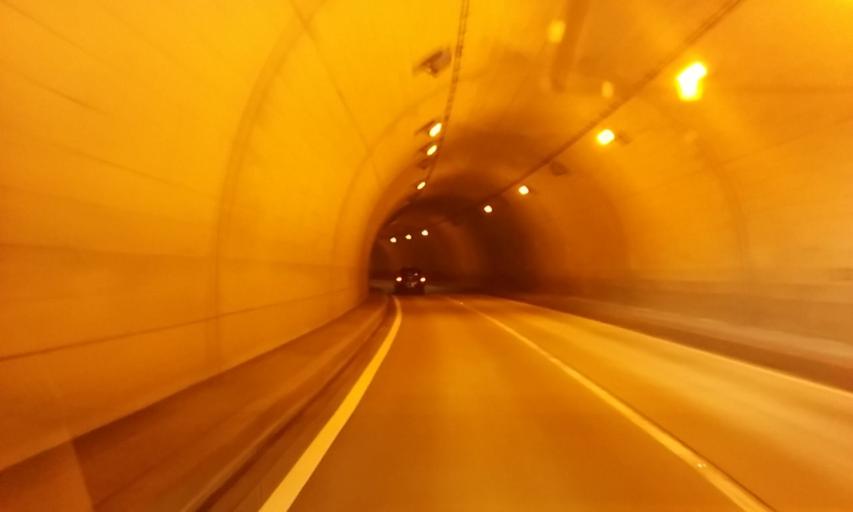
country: JP
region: Kyoto
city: Miyazu
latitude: 35.5822
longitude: 135.1171
